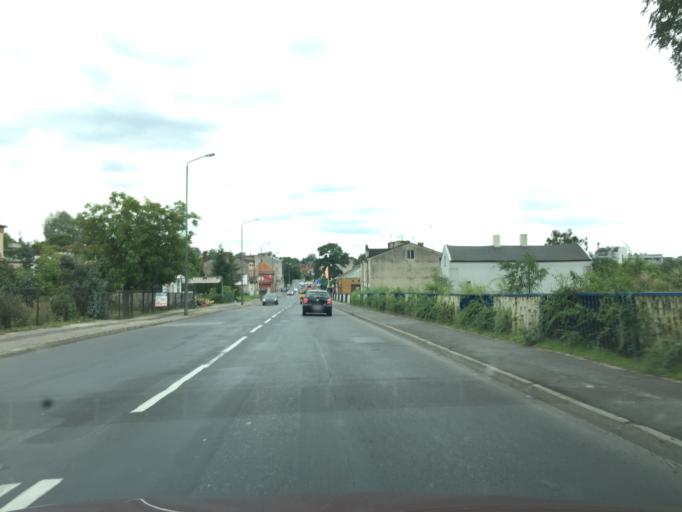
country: PL
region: Greater Poland Voivodeship
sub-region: Kalisz
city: Kalisz
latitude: 51.7731
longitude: 18.0911
